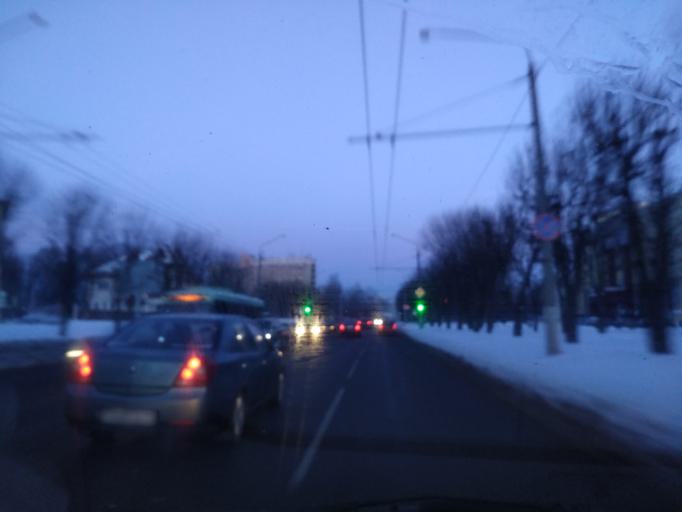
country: BY
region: Mogilev
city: Mahilyow
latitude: 53.8933
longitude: 30.3083
